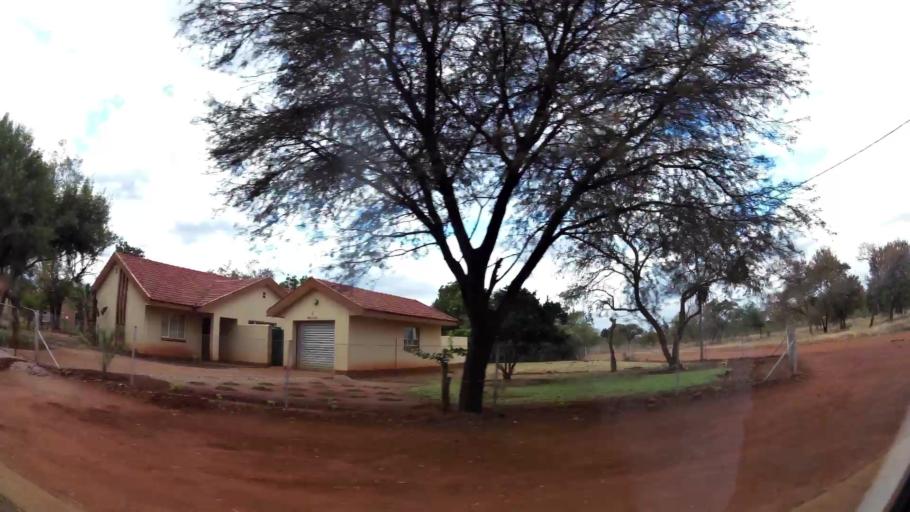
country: ZA
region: Limpopo
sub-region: Waterberg District Municipality
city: Modimolle
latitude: -24.5053
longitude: 28.7197
